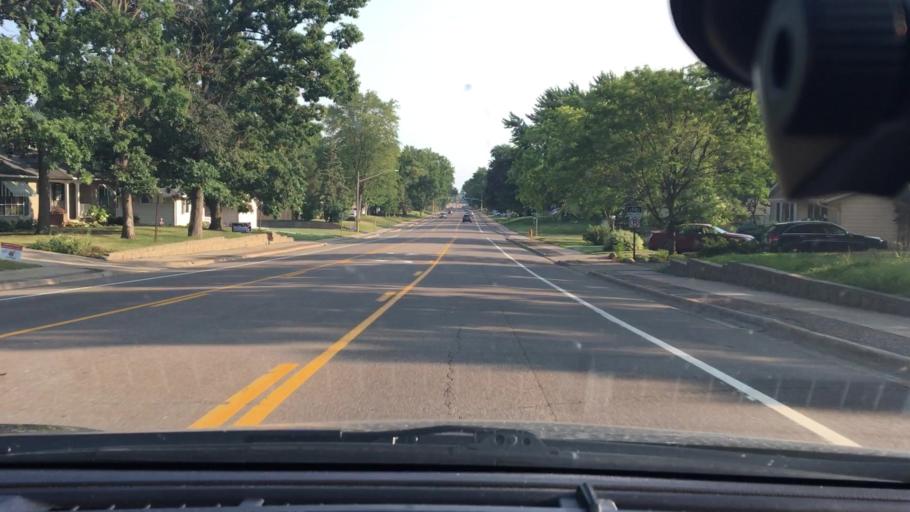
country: US
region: Minnesota
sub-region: Hennepin County
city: Golden Valley
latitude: 44.9961
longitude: -93.3804
